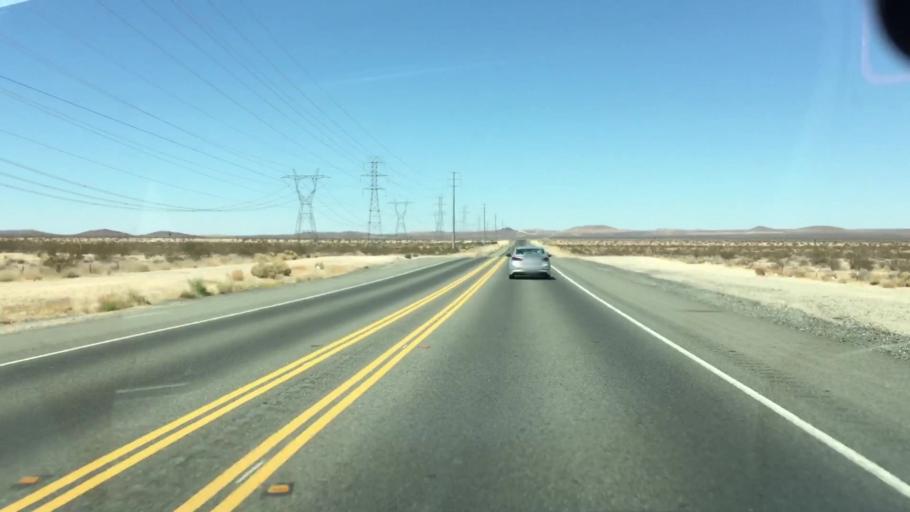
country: US
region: California
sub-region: San Bernardino County
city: Adelanto
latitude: 34.7851
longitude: -117.4823
